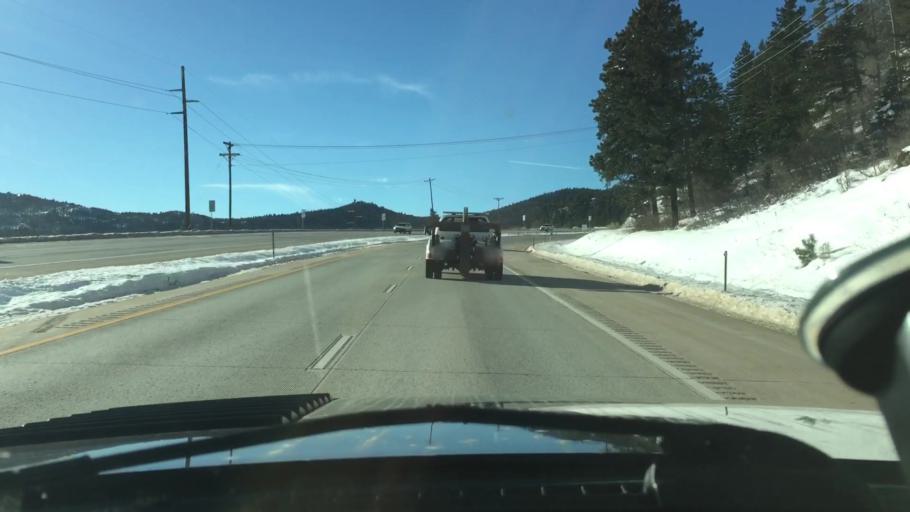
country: US
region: Colorado
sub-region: Jefferson County
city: Indian Hills
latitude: 39.5556
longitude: -105.2401
